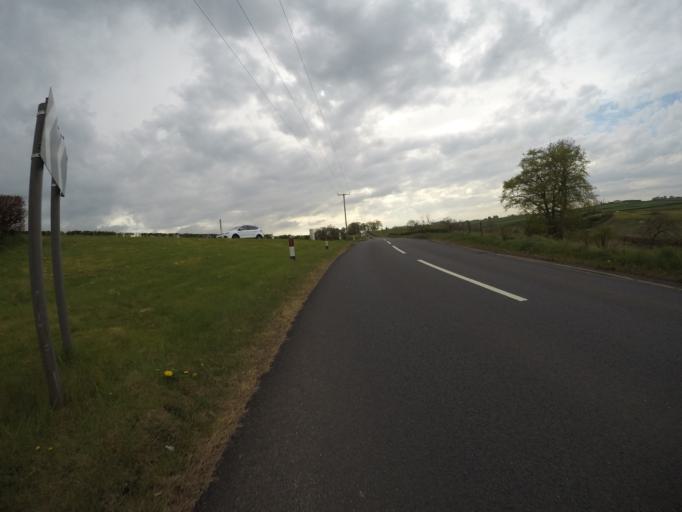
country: GB
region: Scotland
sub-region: East Ayrshire
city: Kilmaurs
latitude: 55.6434
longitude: -4.5041
